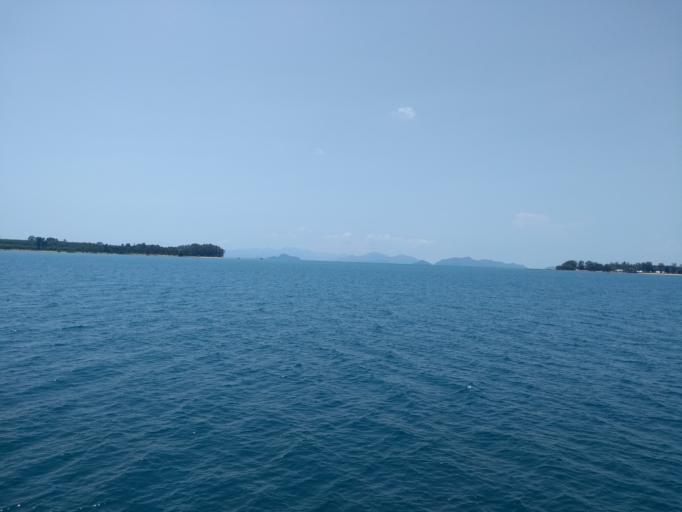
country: TH
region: Trat
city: Ko Kut
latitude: 11.8158
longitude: 102.5233
